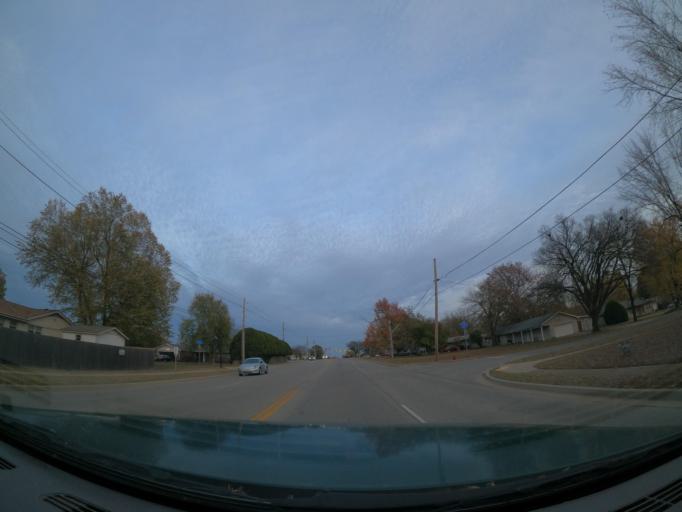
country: US
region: Oklahoma
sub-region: Tulsa County
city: Broken Arrow
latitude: 36.0319
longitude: -95.7932
